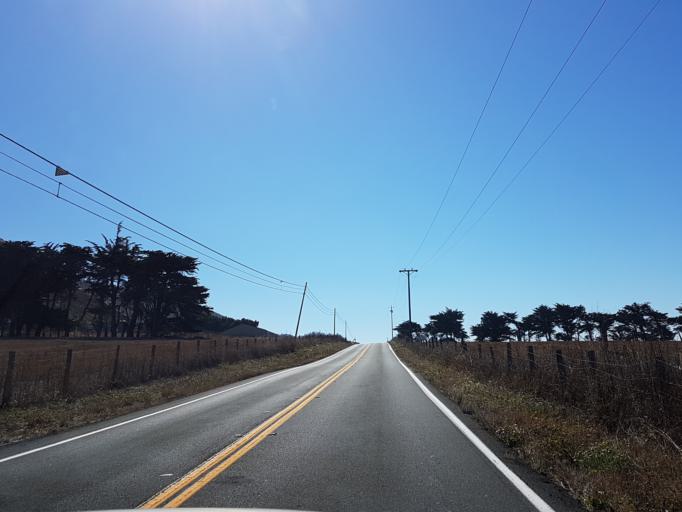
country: US
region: California
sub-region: Mendocino County
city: Boonville
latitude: 39.0836
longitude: -123.6979
